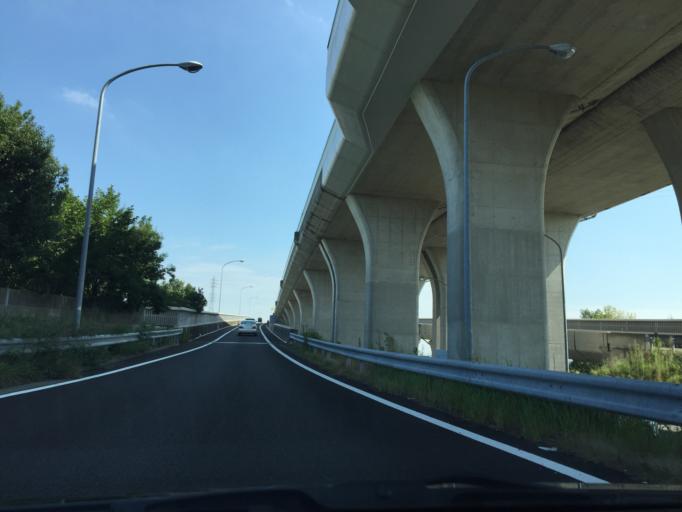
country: JP
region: Aichi
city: Ichinomiya
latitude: 35.3140
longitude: 136.7758
